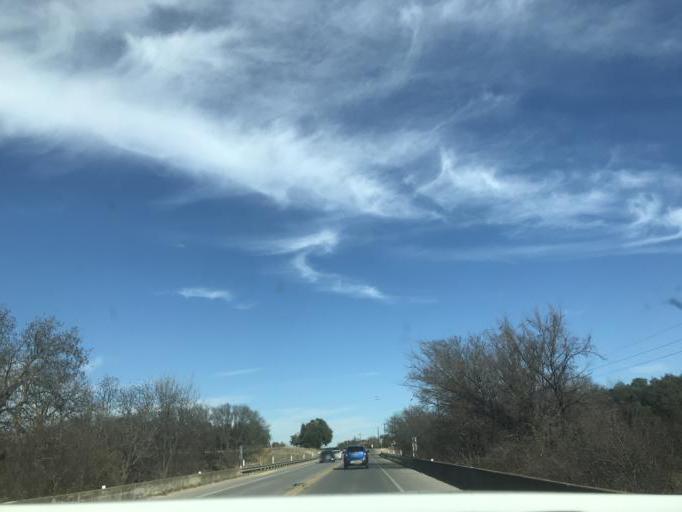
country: US
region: Texas
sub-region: Erath County
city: Stephenville
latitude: 32.2350
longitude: -98.2042
